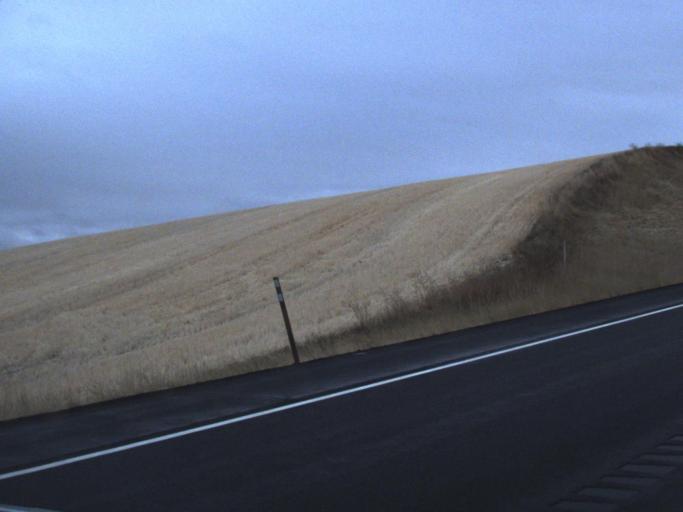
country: US
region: Washington
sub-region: Spokane County
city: Cheney
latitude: 47.3633
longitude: -117.3808
